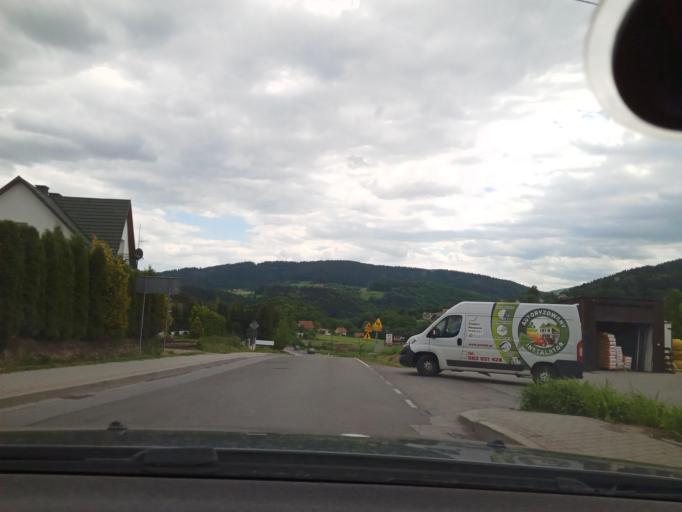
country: PL
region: Lesser Poland Voivodeship
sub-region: Powiat limanowski
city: Tymbark
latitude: 49.7595
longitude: 20.3417
